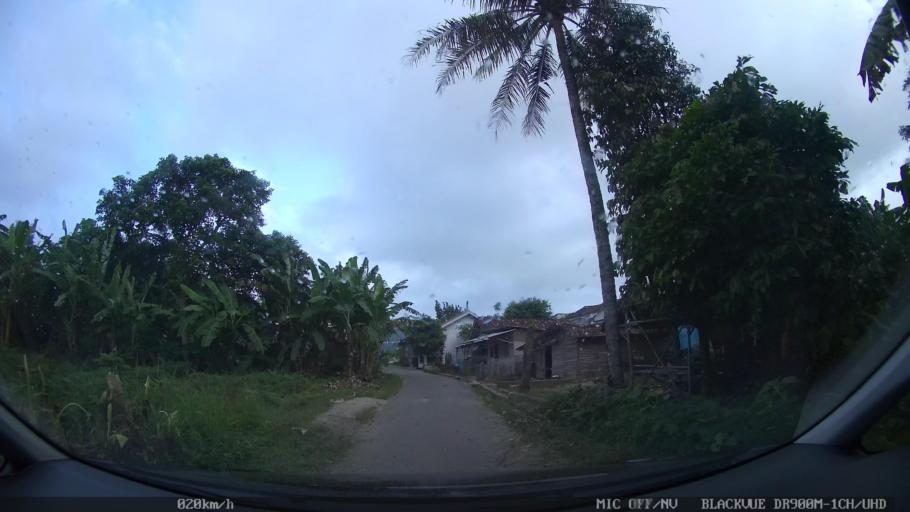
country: ID
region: Lampung
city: Bandarlampung
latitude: -5.4200
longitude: 105.2912
